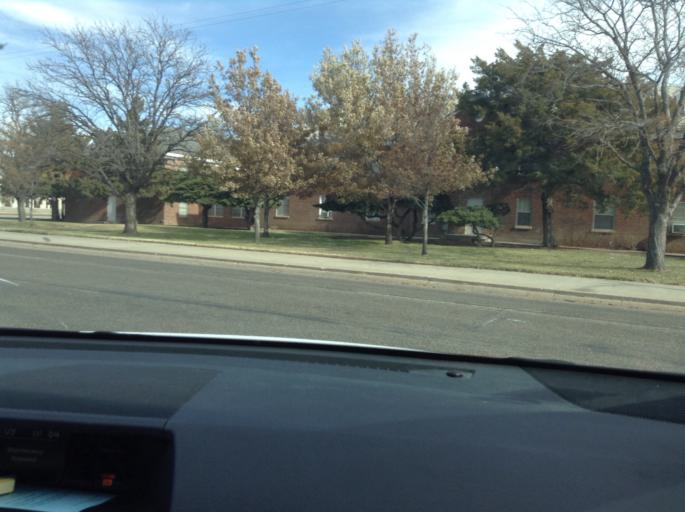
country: US
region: Texas
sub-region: Randall County
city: Canyon
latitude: 34.9840
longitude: -101.9194
